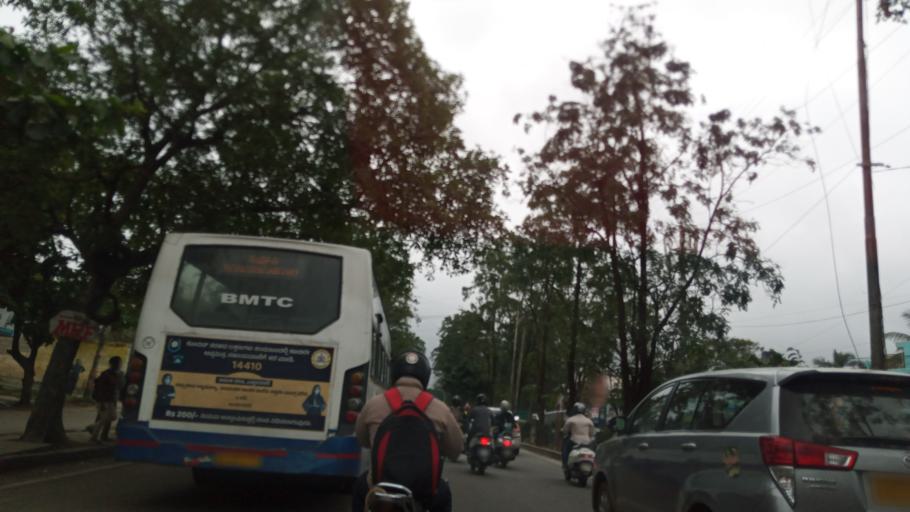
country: IN
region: Karnataka
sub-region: Bangalore Urban
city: Bangalore
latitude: 12.9353
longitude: 77.5366
